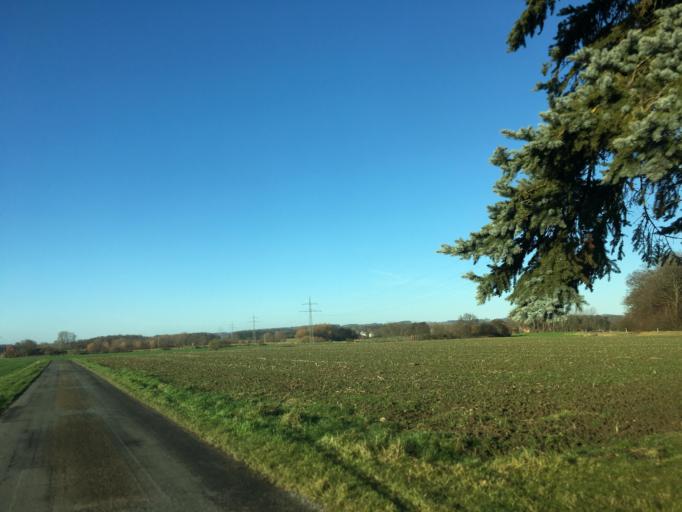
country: DE
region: North Rhine-Westphalia
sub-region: Regierungsbezirk Munster
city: Dulmen
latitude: 51.8683
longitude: 7.2862
